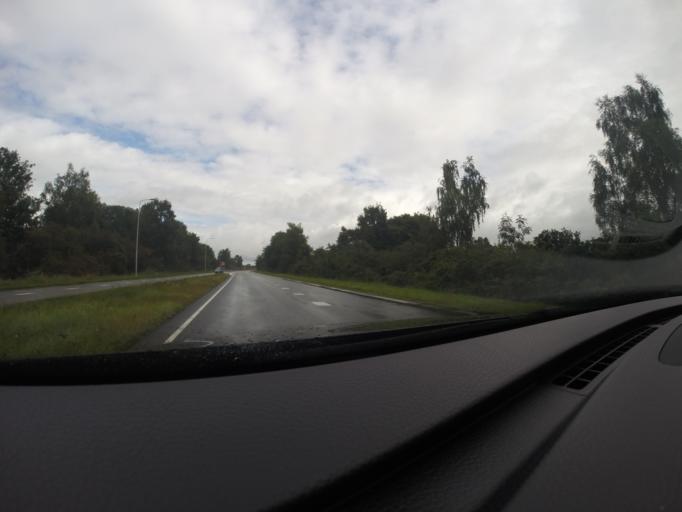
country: NL
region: Gelderland
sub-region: Gemeente Lochem
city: Laren
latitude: 52.2510
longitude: 6.3988
